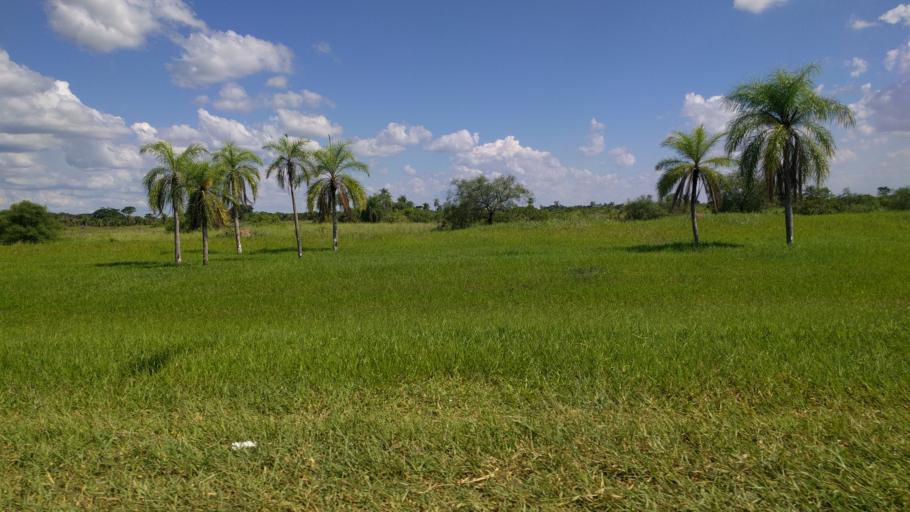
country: BO
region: Santa Cruz
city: La Belgica
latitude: -17.6552
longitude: -63.1533
